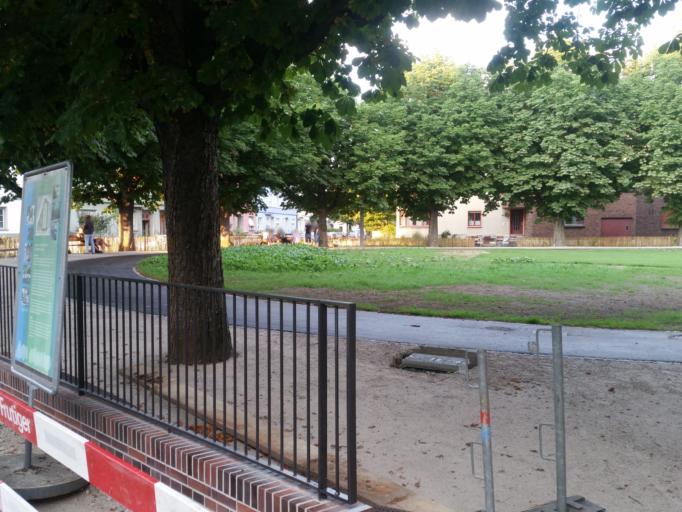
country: CH
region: Basel-City
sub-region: Basel-Stadt
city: Basel
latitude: 47.5580
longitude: 7.5693
